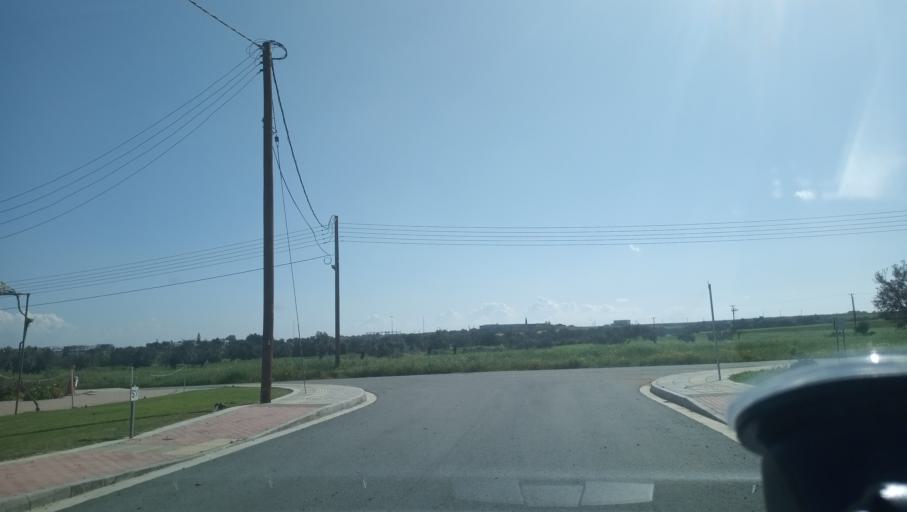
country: CY
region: Lefkosia
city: Tseri
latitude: 35.0882
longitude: 33.3071
